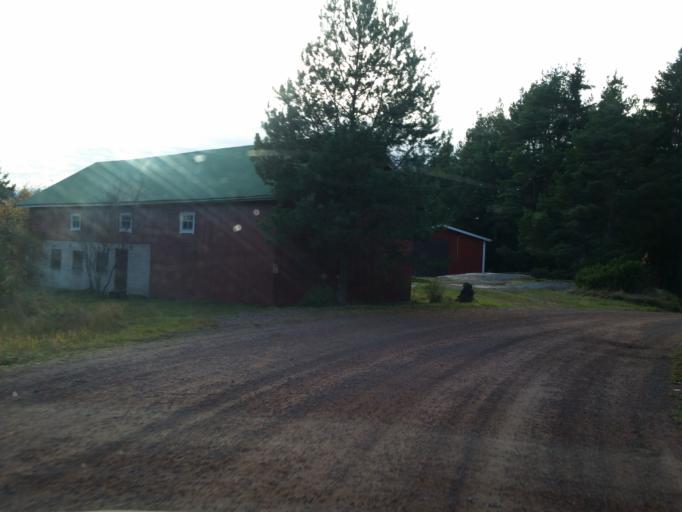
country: AX
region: Alands skaergard
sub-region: Kumlinge
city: Kumlinge
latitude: 60.2535
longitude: 20.7631
